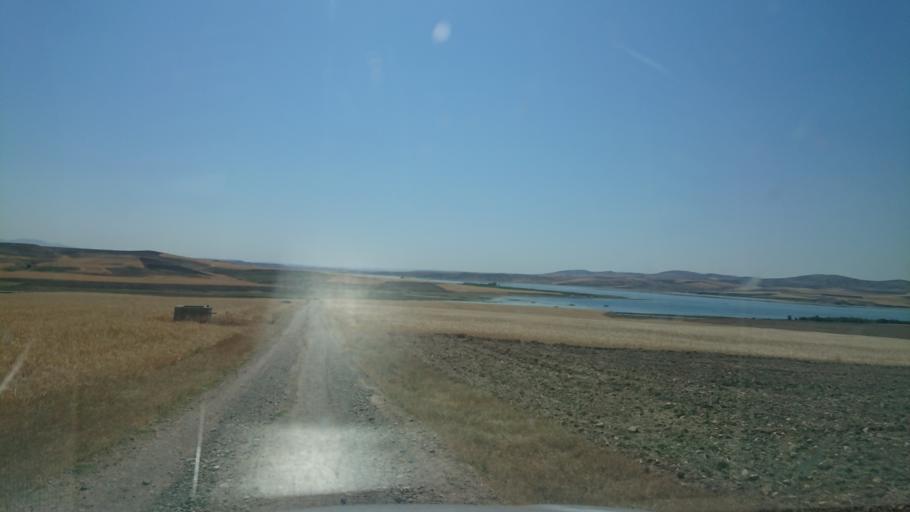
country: TR
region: Aksaray
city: Sariyahsi
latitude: 39.0556
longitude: 33.8925
